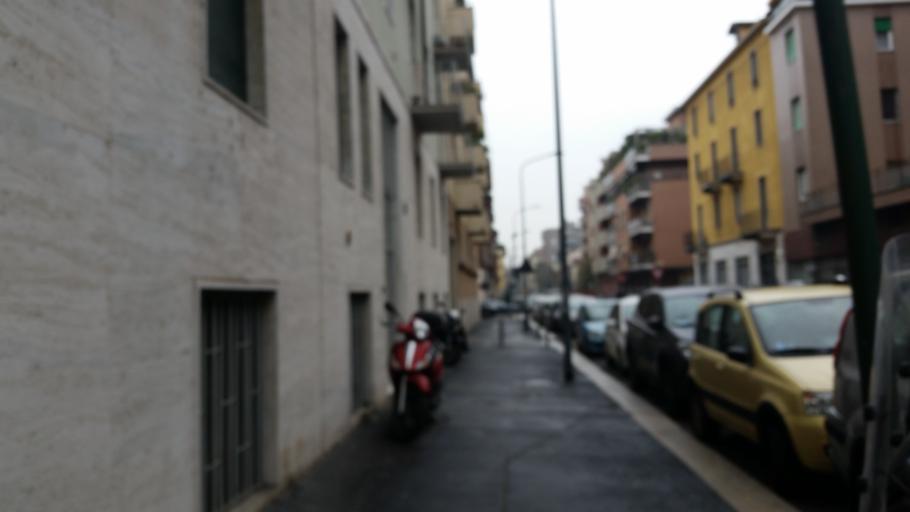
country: IT
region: Lombardy
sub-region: Citta metropolitana di Milano
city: Milano
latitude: 45.4708
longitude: 9.1538
